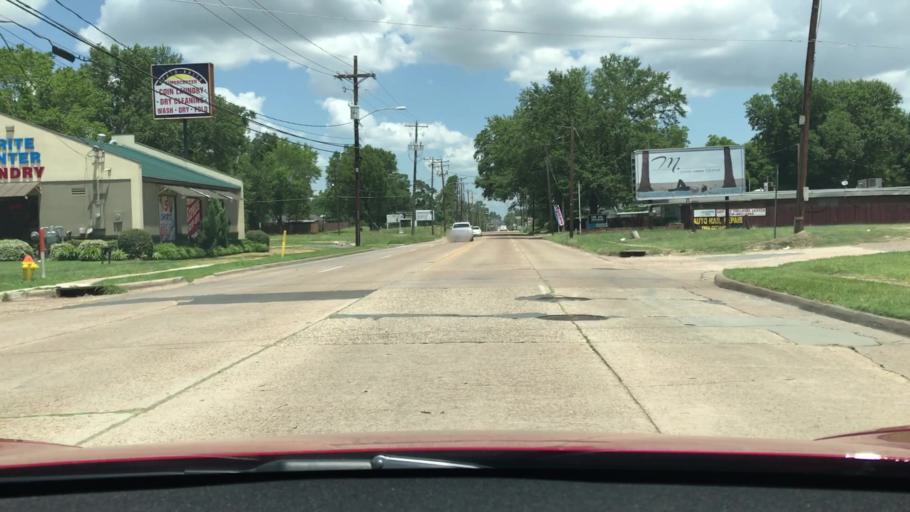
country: US
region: Louisiana
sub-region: Bossier Parish
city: Bossier City
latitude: 32.4430
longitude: -93.7460
